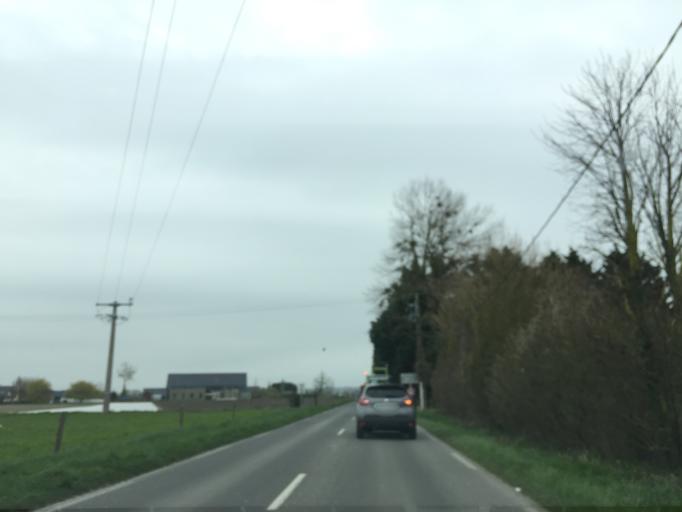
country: FR
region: Brittany
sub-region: Departement d'Ille-et-Vilaine
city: Cherrueix
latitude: 48.6028
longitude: -1.7144
